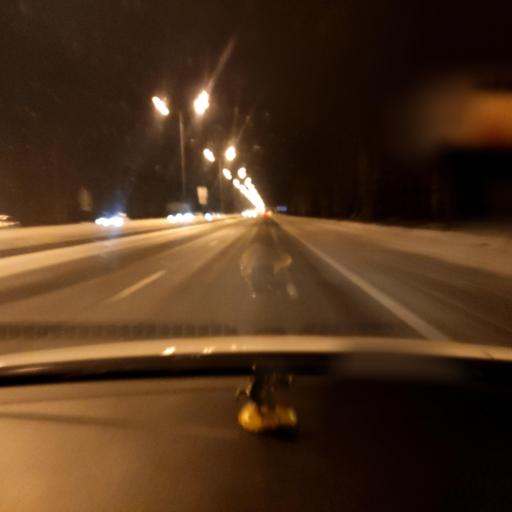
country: RU
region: Tatarstan
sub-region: Zelenodol'skiy Rayon
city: Vasil'yevo
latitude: 55.8693
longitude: 48.7291
